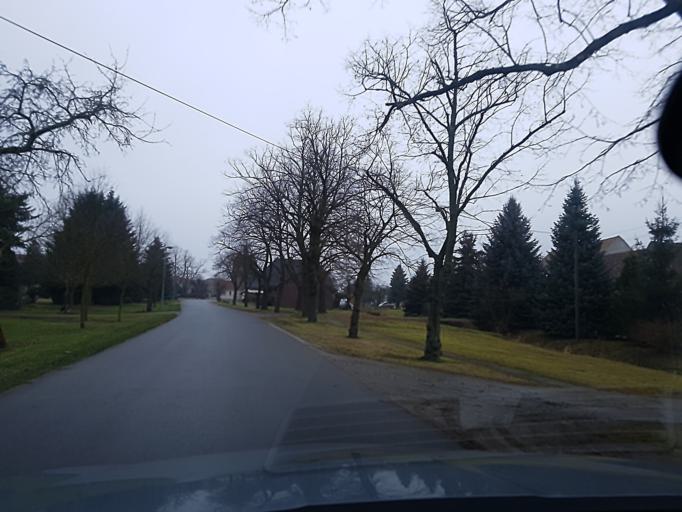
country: DE
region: Brandenburg
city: Schonewalde
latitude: 51.6584
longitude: 13.5950
